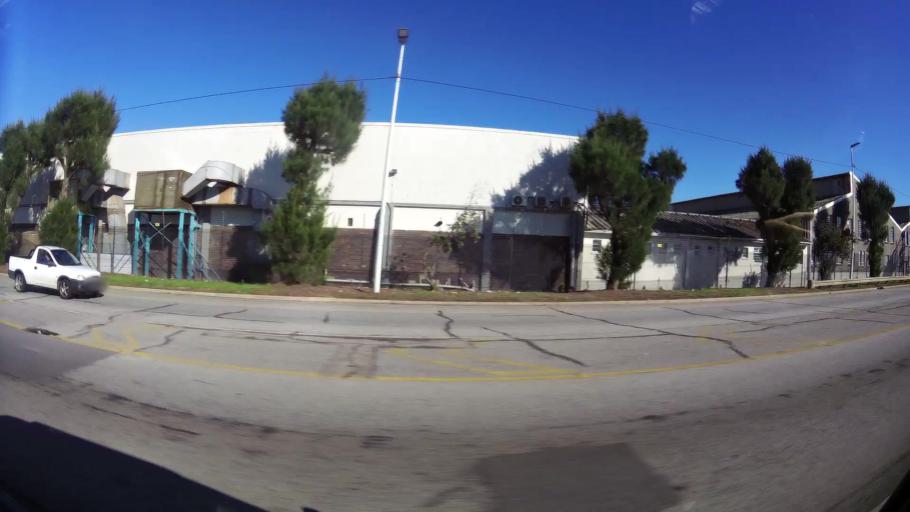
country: ZA
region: Eastern Cape
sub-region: Nelson Mandela Bay Metropolitan Municipality
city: Port Elizabeth
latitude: -33.9400
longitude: 25.6107
